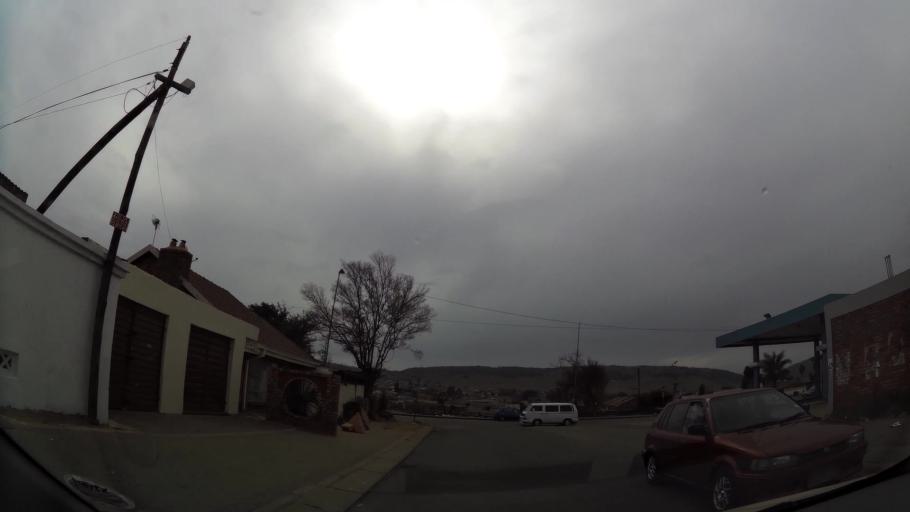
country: ZA
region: Gauteng
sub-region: City of Tshwane Metropolitan Municipality
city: Pretoria
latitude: -25.7114
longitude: 28.3460
